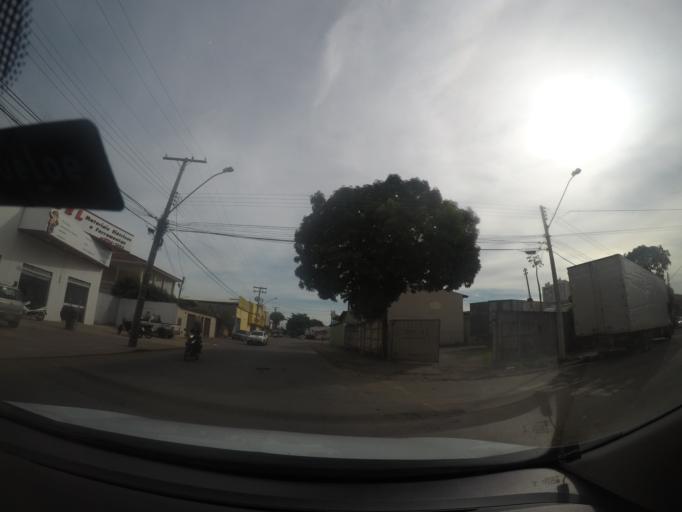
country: BR
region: Goias
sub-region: Goiania
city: Goiania
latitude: -16.6652
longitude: -49.3118
